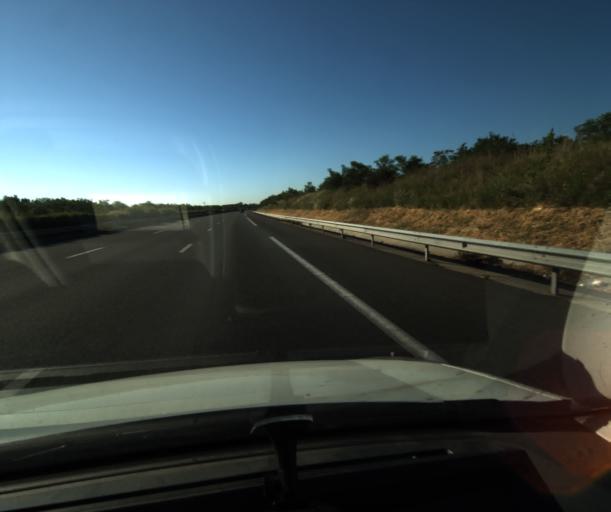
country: FR
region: Midi-Pyrenees
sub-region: Departement du Tarn-et-Garonne
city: Pompignan
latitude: 43.8356
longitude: 1.3360
